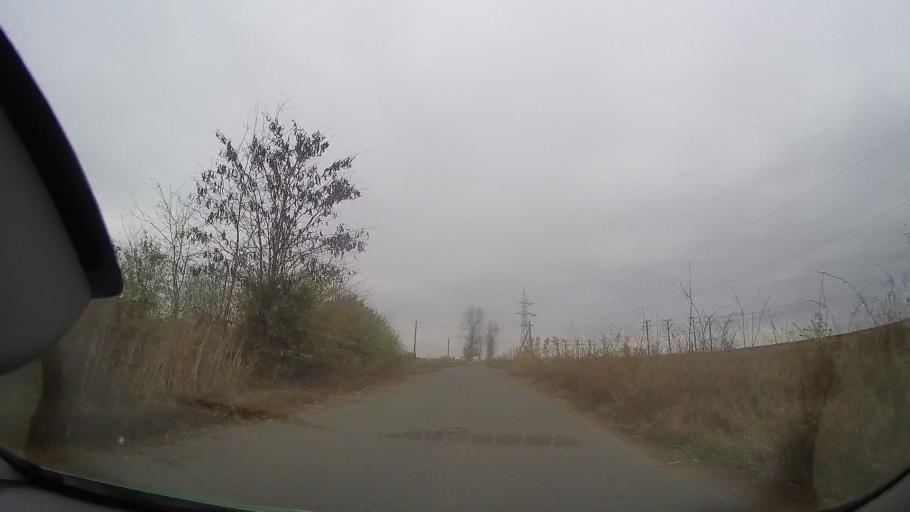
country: RO
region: Braila
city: Dudesti
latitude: 44.8966
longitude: 27.4332
